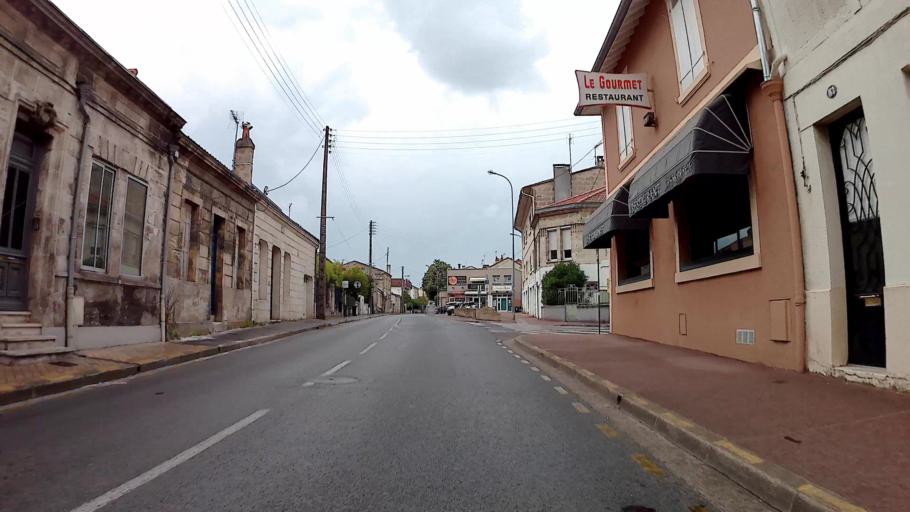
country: FR
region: Aquitaine
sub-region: Departement de la Gironde
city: Le Bouscat
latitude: 44.8561
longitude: -0.6017
